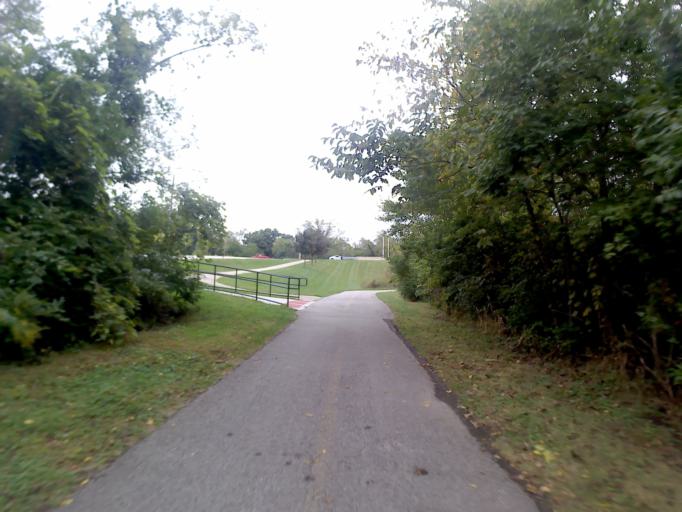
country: US
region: Illinois
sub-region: Kane County
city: North Aurora
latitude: 41.7880
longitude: -88.3182
